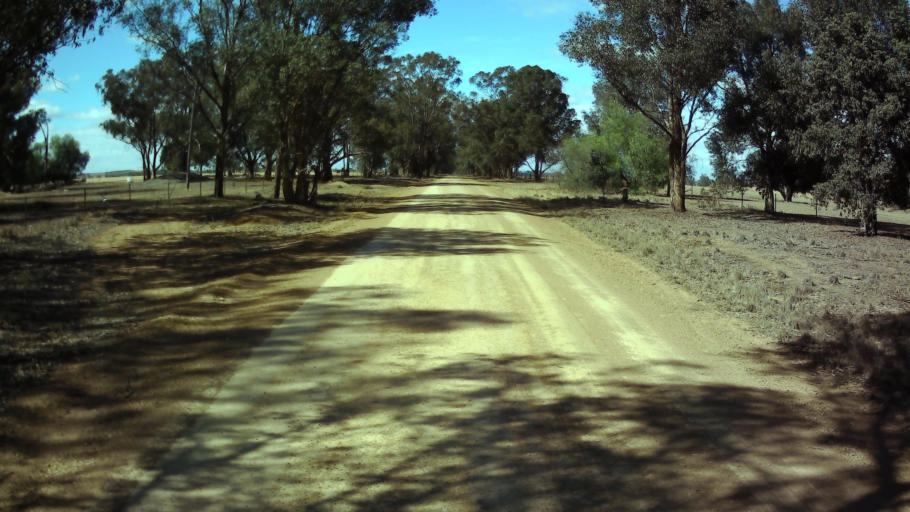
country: AU
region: New South Wales
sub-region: Weddin
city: Grenfell
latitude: -34.0453
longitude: 148.3149
